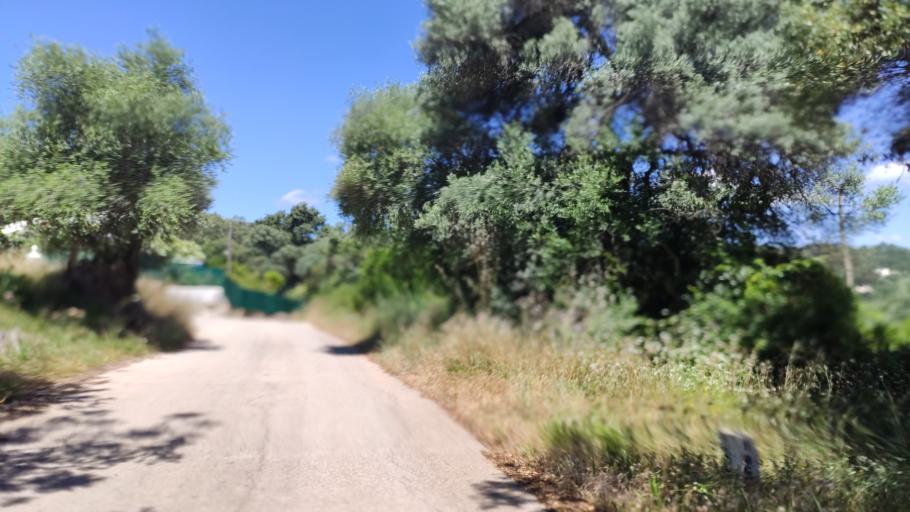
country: PT
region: Faro
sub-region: Sao Bras de Alportel
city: Sao Bras de Alportel
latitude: 37.1711
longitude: -7.9125
